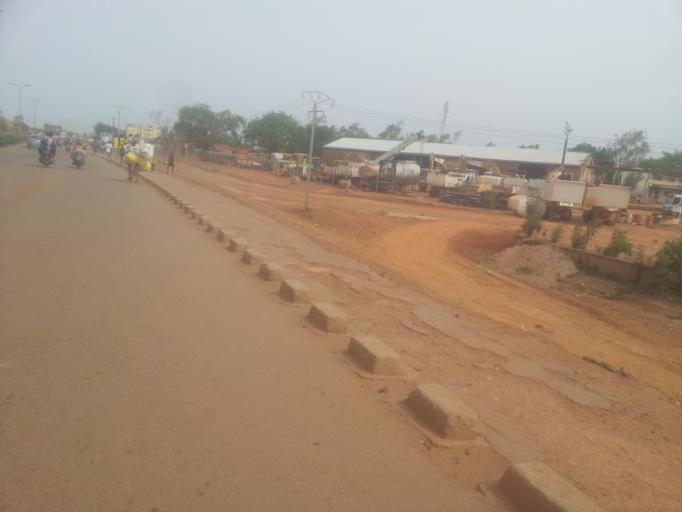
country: BF
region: Centre
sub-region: Kadiogo Province
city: Ouagadougou
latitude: 12.3852
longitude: -1.5559
